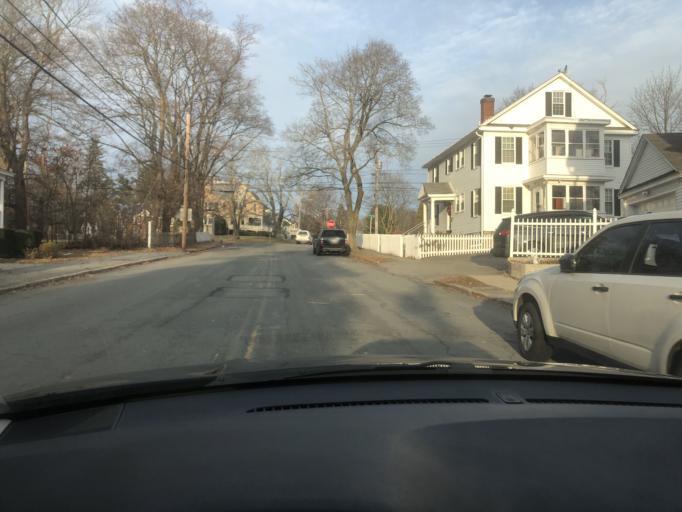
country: US
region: Massachusetts
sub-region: Essex County
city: Lawrence
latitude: 42.7170
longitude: -71.1466
